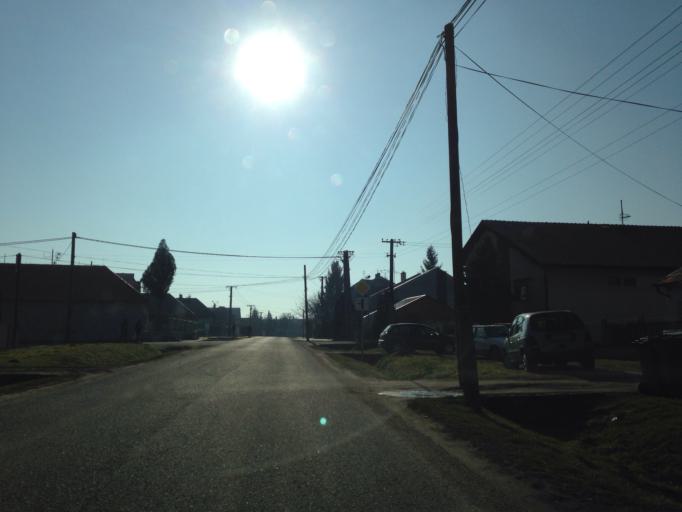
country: SK
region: Nitriansky
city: Svodin
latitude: 47.9258
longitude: 18.4025
